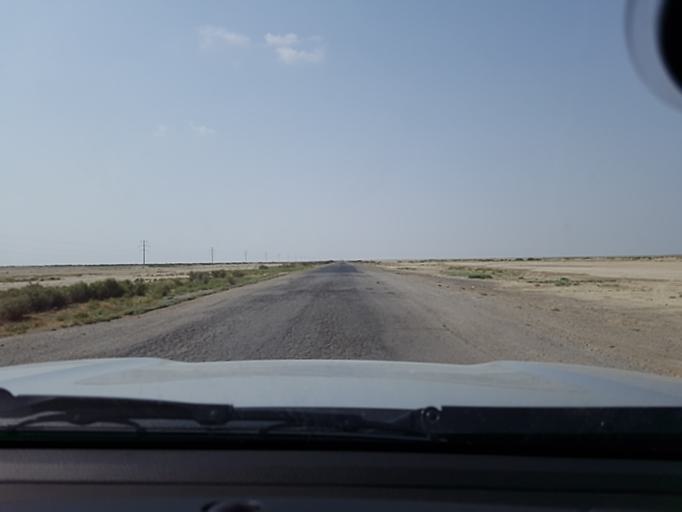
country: TM
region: Balkan
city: Gumdag
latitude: 38.9029
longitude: 54.5922
